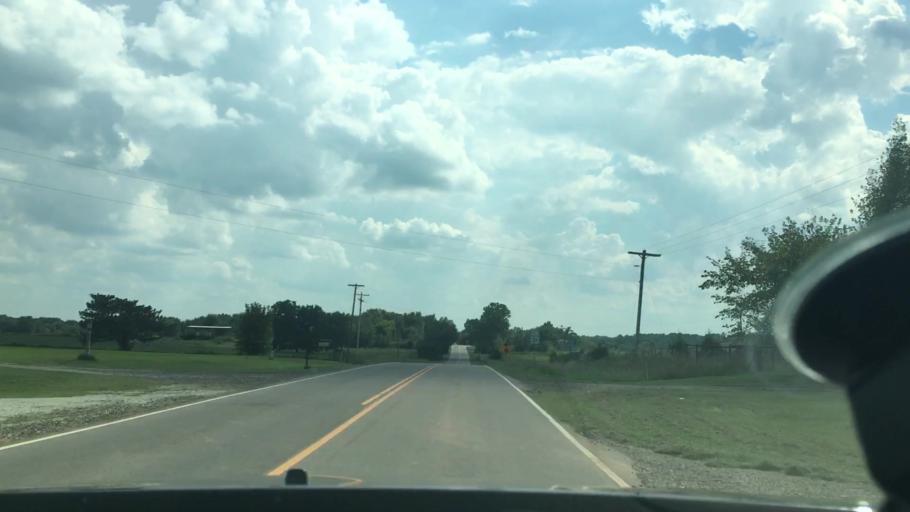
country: US
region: Oklahoma
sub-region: Pottawatomie County
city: Shawnee
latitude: 35.3380
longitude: -96.8072
